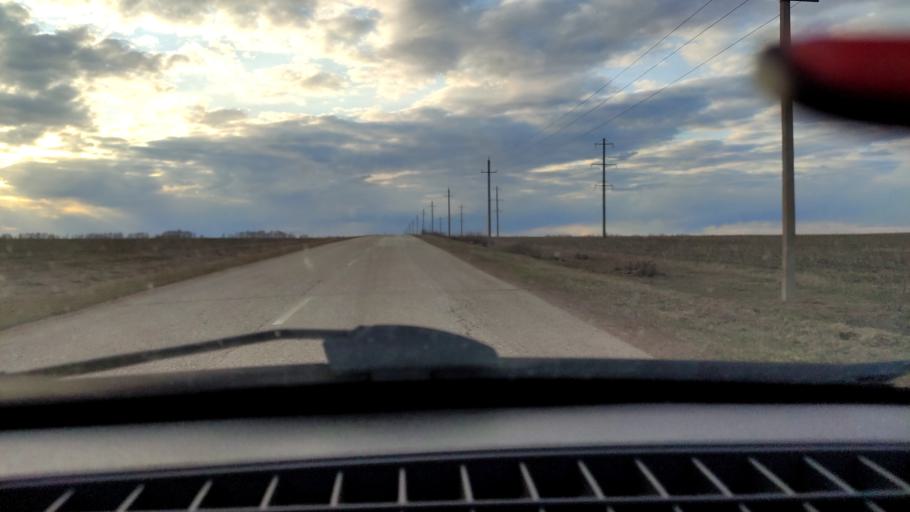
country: RU
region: Bashkortostan
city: Tolbazy
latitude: 54.0038
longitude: 55.7615
